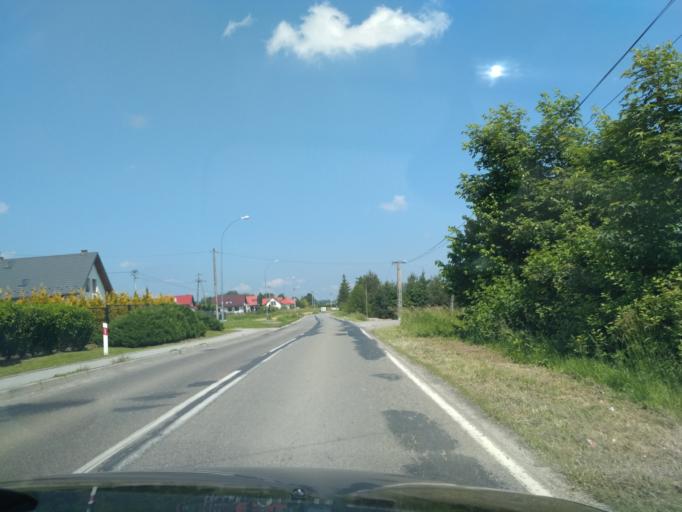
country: PL
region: Subcarpathian Voivodeship
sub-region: Powiat lancucki
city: Albigowa
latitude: 50.0225
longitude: 22.2240
